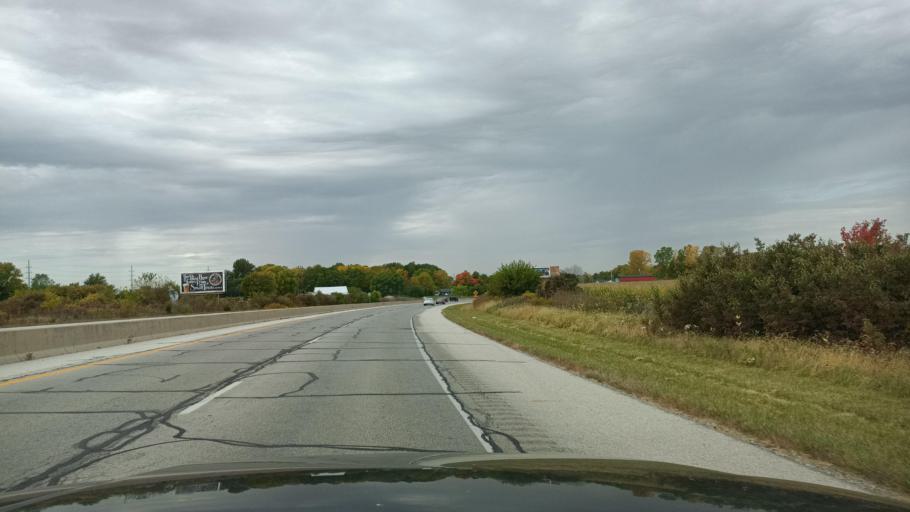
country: US
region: Indiana
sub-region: Delaware County
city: Yorktown
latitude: 40.2192
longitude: -85.5137
